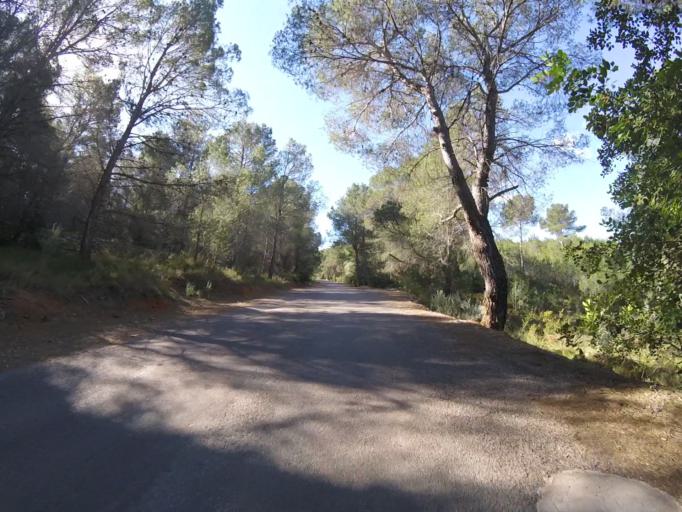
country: ES
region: Valencia
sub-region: Provincia de Castello
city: Orpesa/Oropesa del Mar
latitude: 40.0775
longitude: 0.1176
